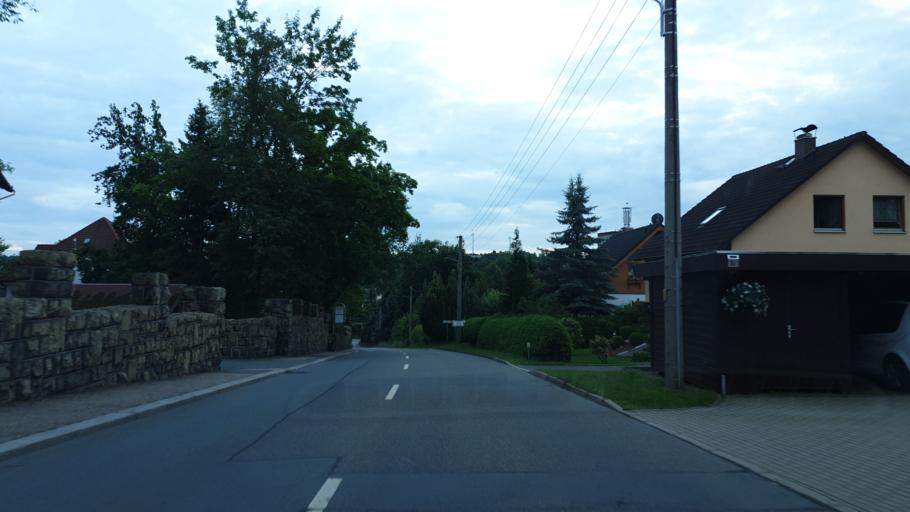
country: DE
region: Saxony
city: Hohenstein-Ernstthal
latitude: 50.7884
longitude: 12.7227
